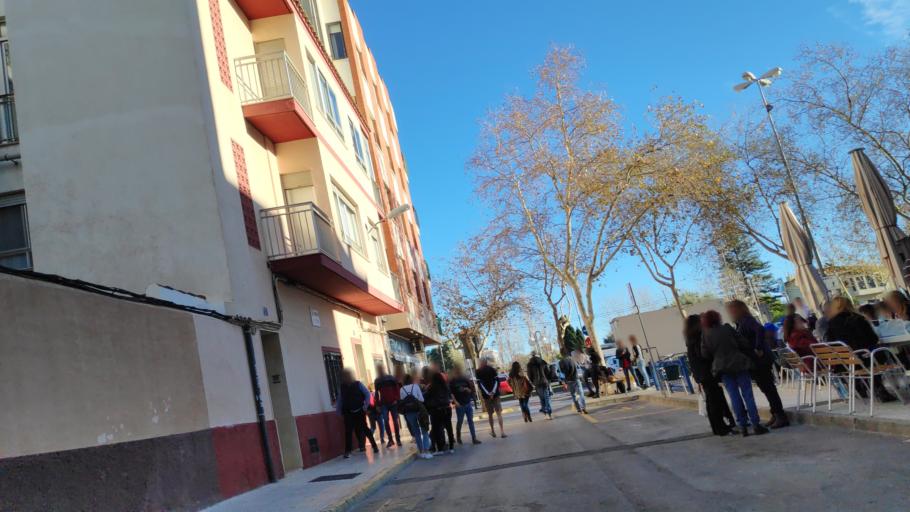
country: ES
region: Valencia
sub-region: Provincia de Castello
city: Benicassim
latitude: 40.0547
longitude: 0.0648
